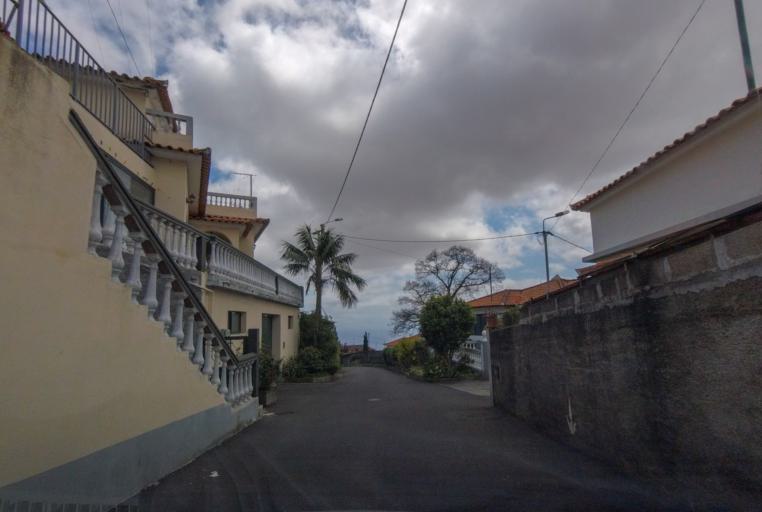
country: PT
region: Madeira
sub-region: Funchal
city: Nossa Senhora do Monte
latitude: 32.6807
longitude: -16.9122
